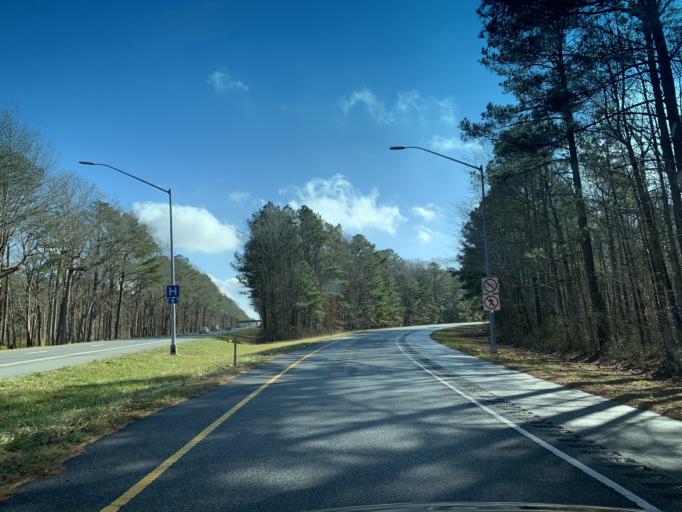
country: US
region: Maryland
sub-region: Worcester County
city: Berlin
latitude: 38.3715
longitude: -75.2761
